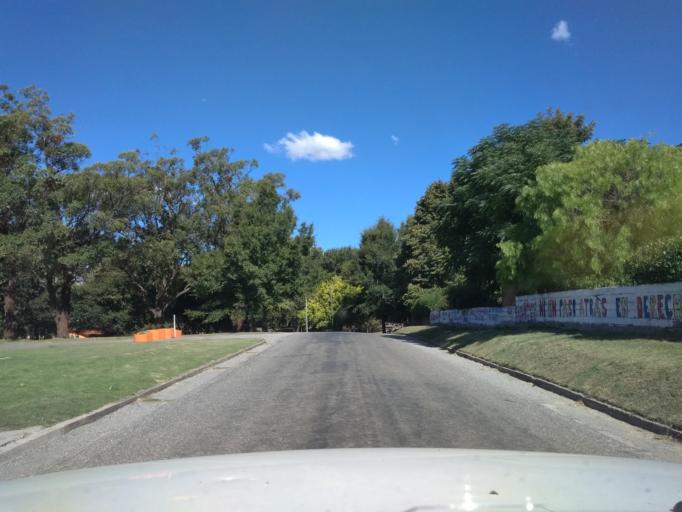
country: UY
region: Florida
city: Florida
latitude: -34.0983
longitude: -56.2071
